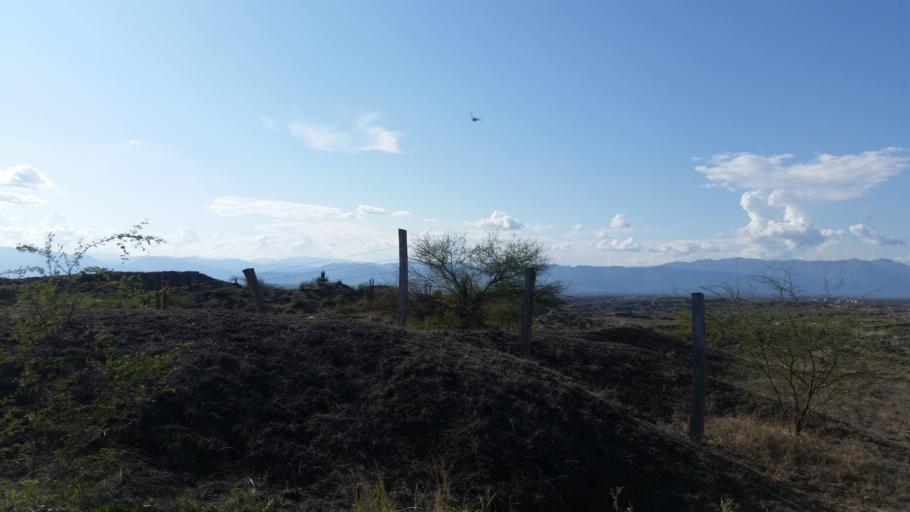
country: CO
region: Huila
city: Villavieja
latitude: 3.2329
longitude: -75.1232
